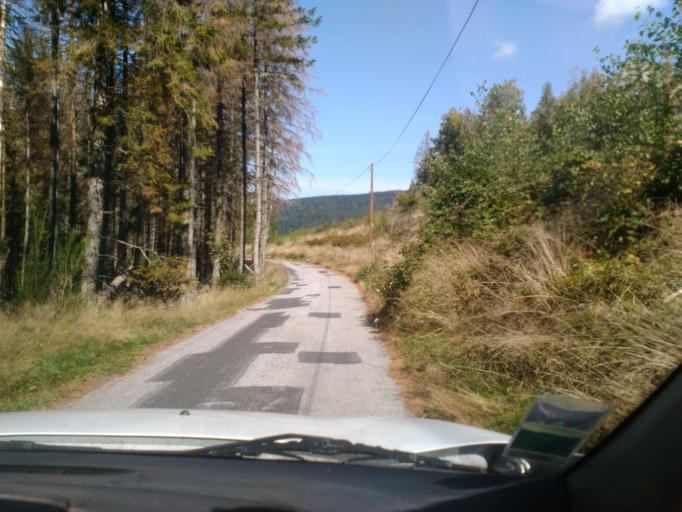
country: FR
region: Lorraine
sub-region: Departement des Vosges
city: Le Tholy
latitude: 48.0713
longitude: 6.7884
